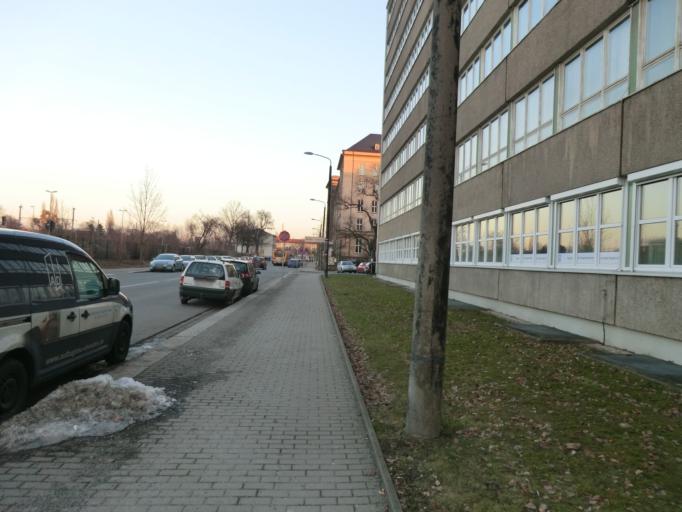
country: DE
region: Saxony
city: Dresden
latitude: 51.0348
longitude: 13.7458
